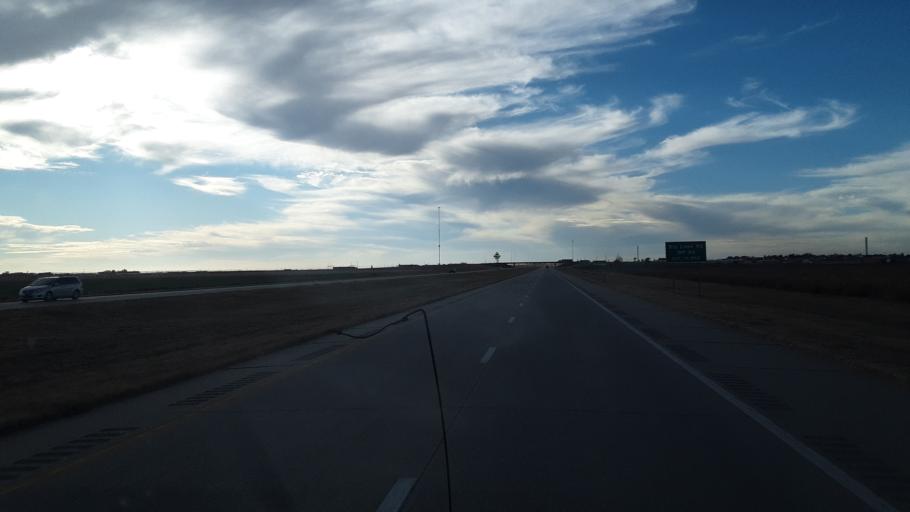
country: US
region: Kansas
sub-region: Finney County
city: Holcomb
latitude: 38.0034
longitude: -100.9816
